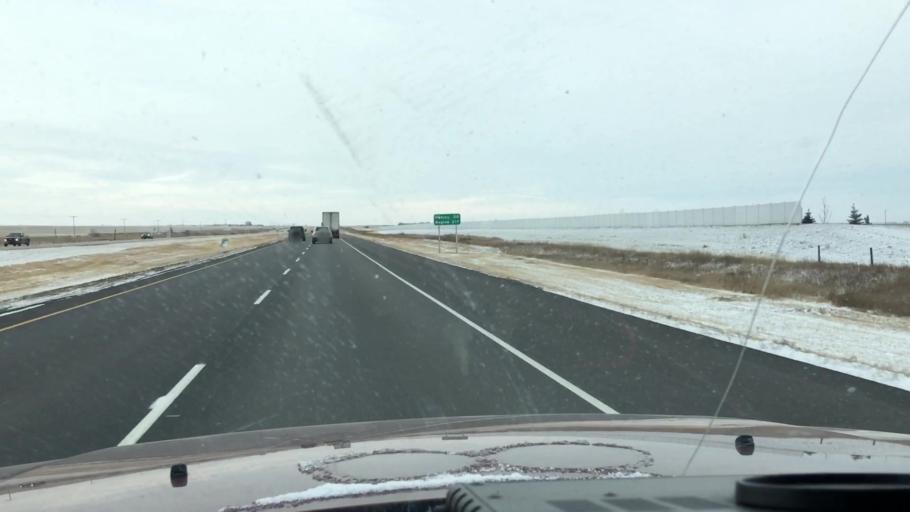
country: CA
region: Saskatchewan
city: Saskatoon
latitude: 51.8075
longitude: -106.4942
